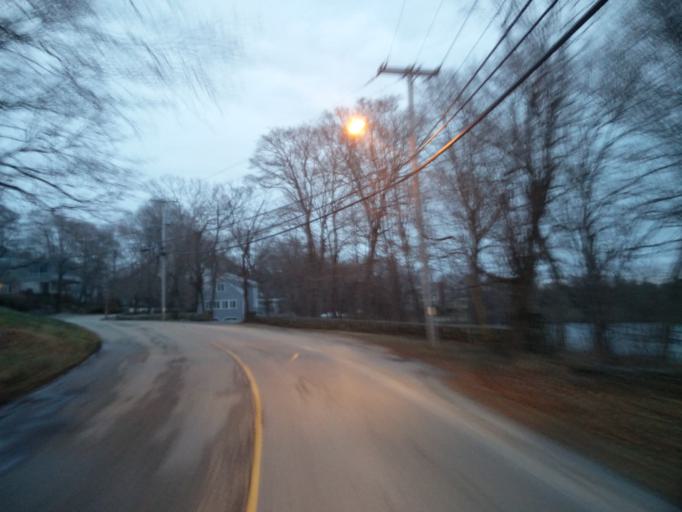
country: US
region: Massachusetts
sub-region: Norfolk County
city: Cohasset
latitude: 42.2632
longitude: -70.8342
